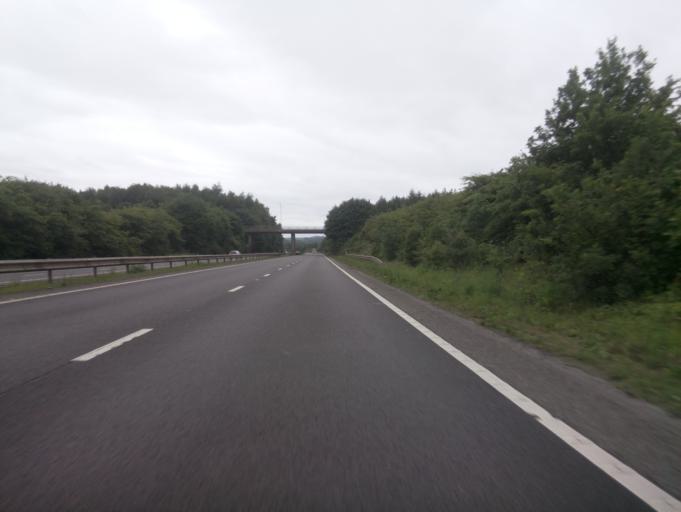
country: GB
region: England
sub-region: Leicestershire
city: Castle Donington
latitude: 52.7985
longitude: -1.3679
